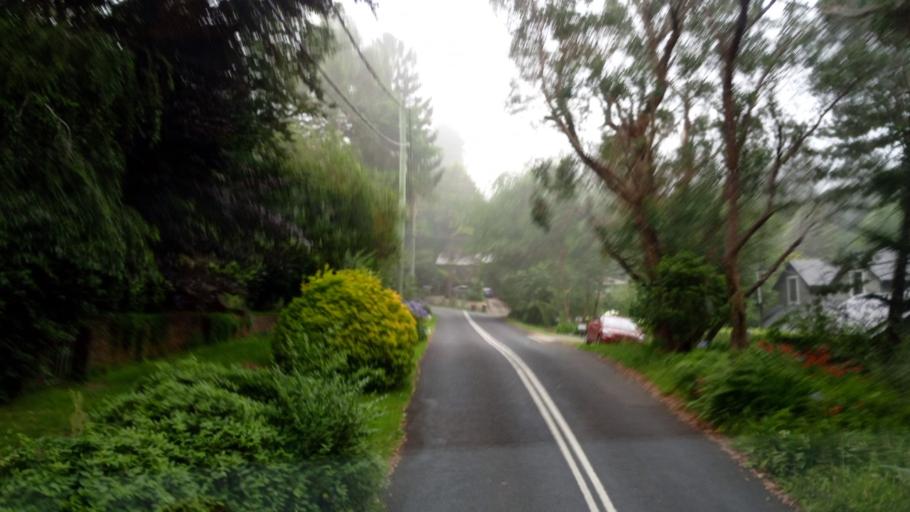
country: AU
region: New South Wales
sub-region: Blue Mountains Municipality
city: Leura
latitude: -33.7176
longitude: 150.3392
